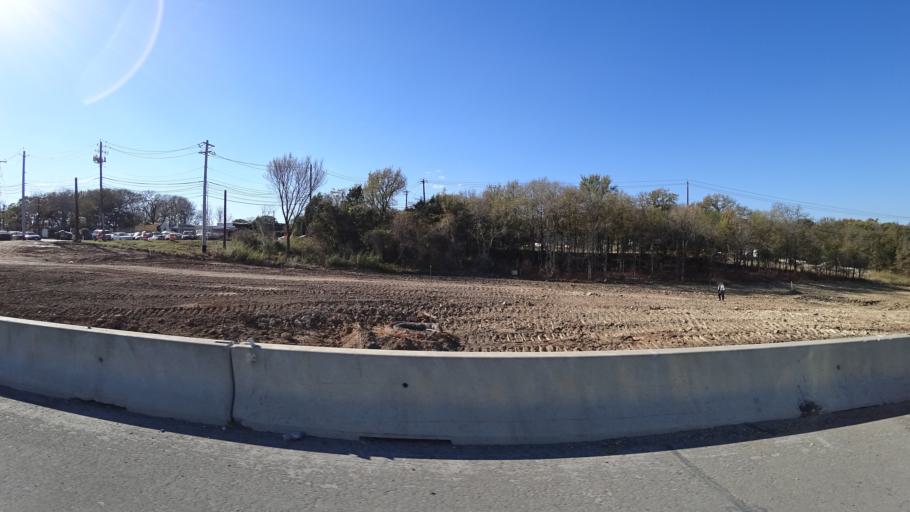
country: US
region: Texas
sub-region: Travis County
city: Austin
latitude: 30.2714
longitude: -97.6693
